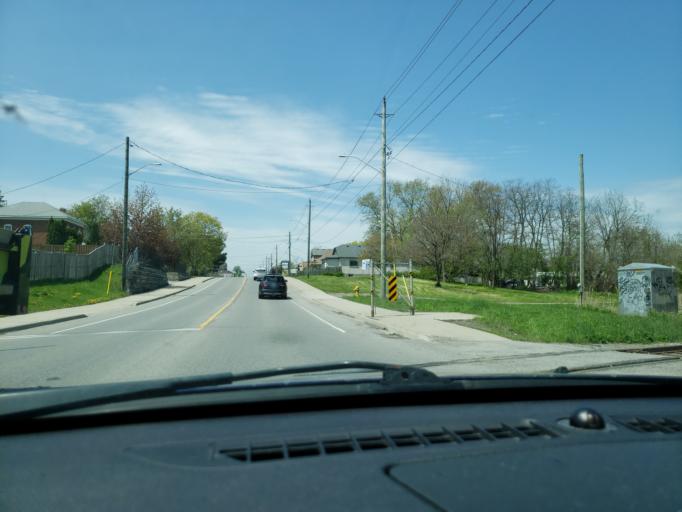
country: CA
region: Ontario
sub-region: Regional Municipality of Niagara
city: St. Catharines
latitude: 43.1608
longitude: -79.2210
